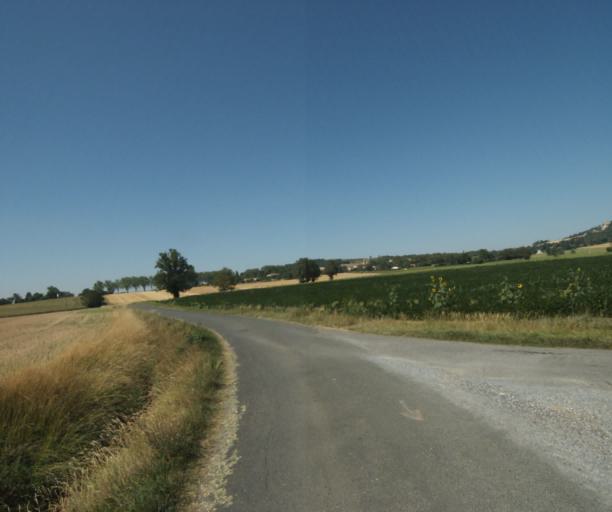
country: FR
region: Midi-Pyrenees
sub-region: Departement de la Haute-Garonne
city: Revel
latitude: 43.5057
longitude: 1.9570
